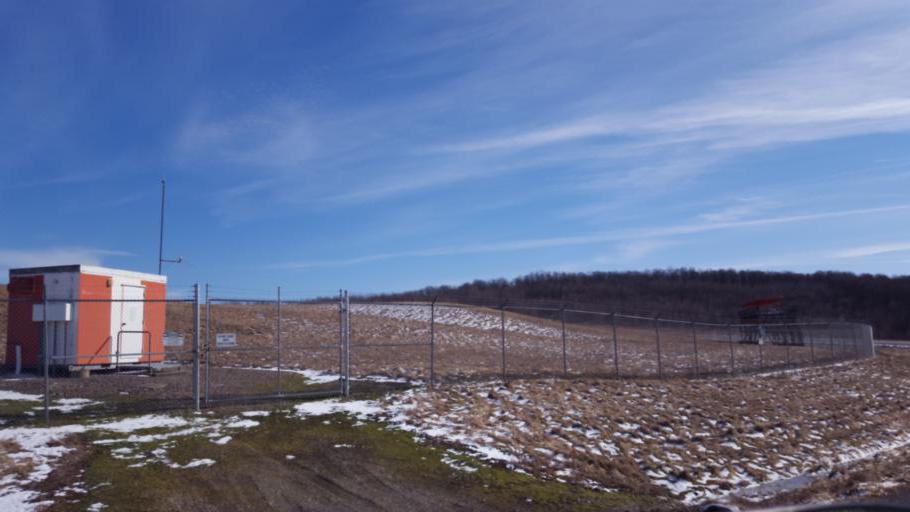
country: US
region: New York
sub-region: Allegany County
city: Wellsville
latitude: 42.1104
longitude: -78.0003
